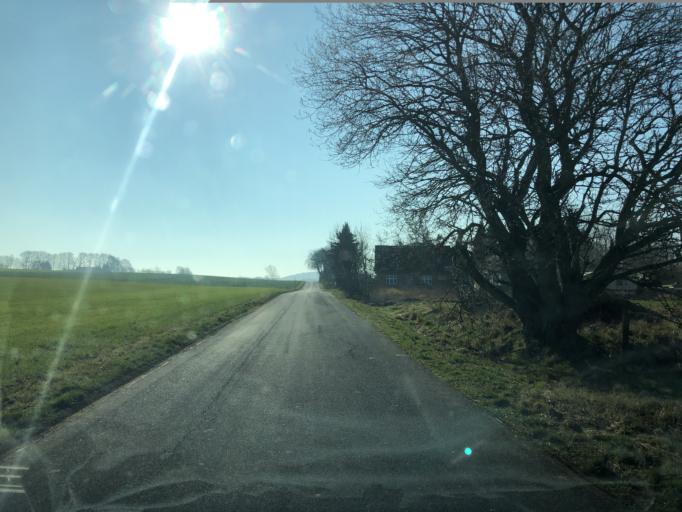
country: DK
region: Central Jutland
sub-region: Favrskov Kommune
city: Hammel
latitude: 56.2028
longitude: 9.8109
